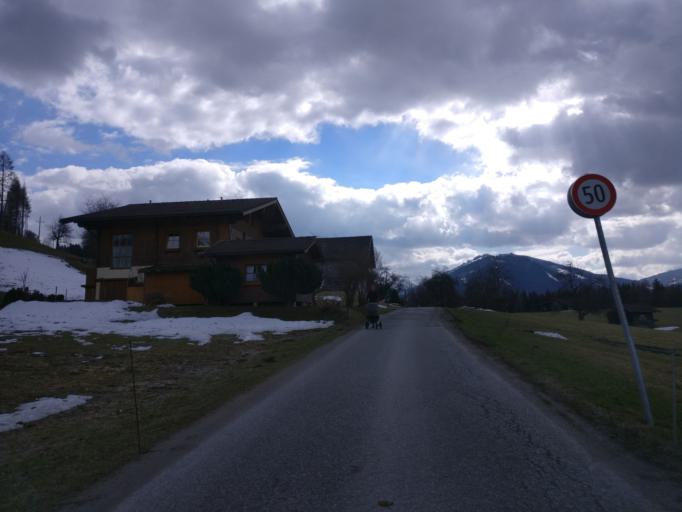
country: AT
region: Salzburg
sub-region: Politischer Bezirk Sankt Johann im Pongau
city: Bischofshofen
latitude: 47.4183
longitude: 13.2311
